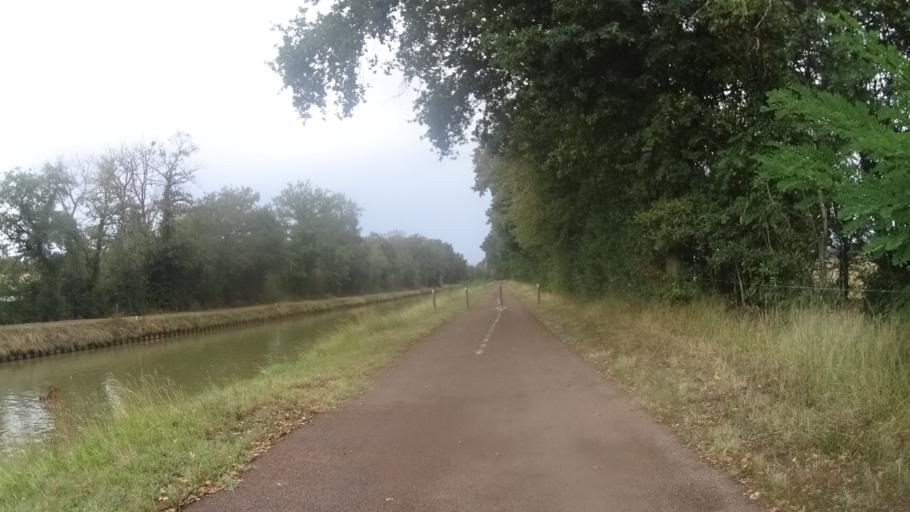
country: FR
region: Bourgogne
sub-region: Departement de la Nievre
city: Imphy
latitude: 46.8971
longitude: 3.2458
